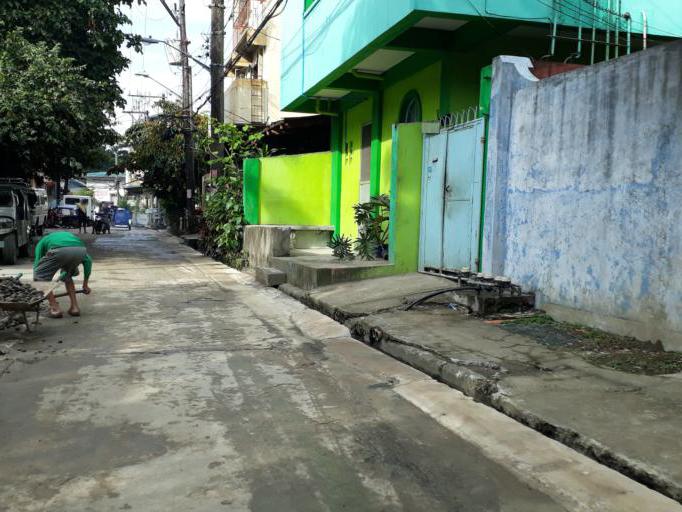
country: PH
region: Calabarzon
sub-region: Province of Rizal
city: Valenzuela
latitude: 14.6747
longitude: 120.9903
